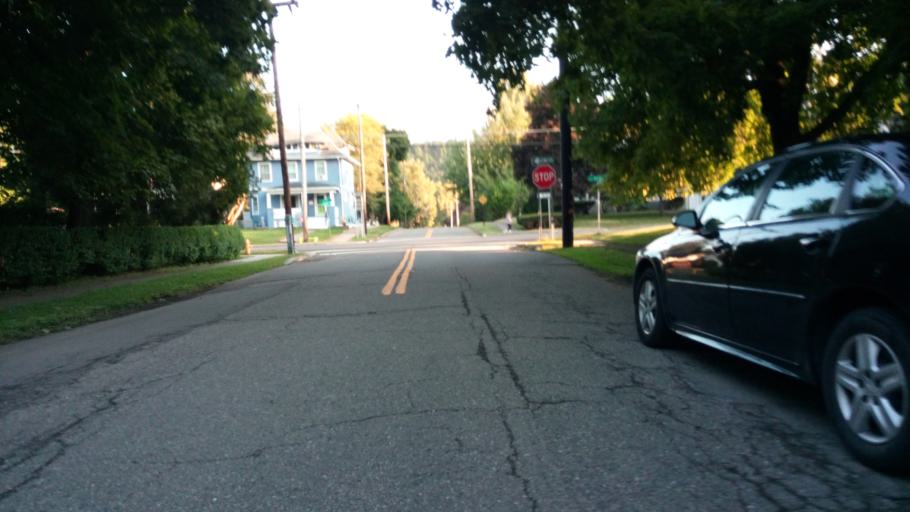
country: US
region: New York
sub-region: Chemung County
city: West Elmira
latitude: 42.0796
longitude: -76.8368
